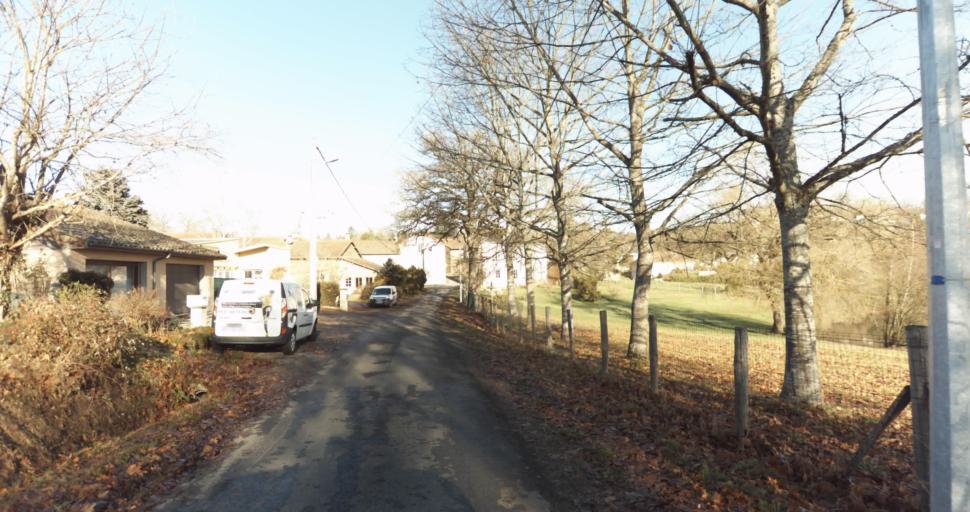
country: FR
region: Limousin
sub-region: Departement de la Haute-Vienne
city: Aixe-sur-Vienne
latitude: 45.8048
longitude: 1.1505
